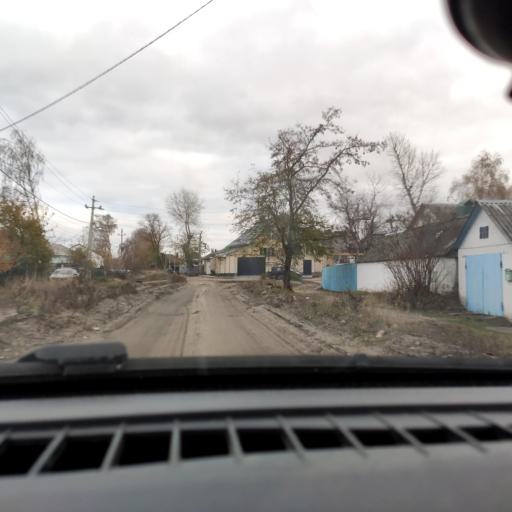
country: RU
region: Voronezj
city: Podgornoye
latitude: 51.7346
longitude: 39.1414
